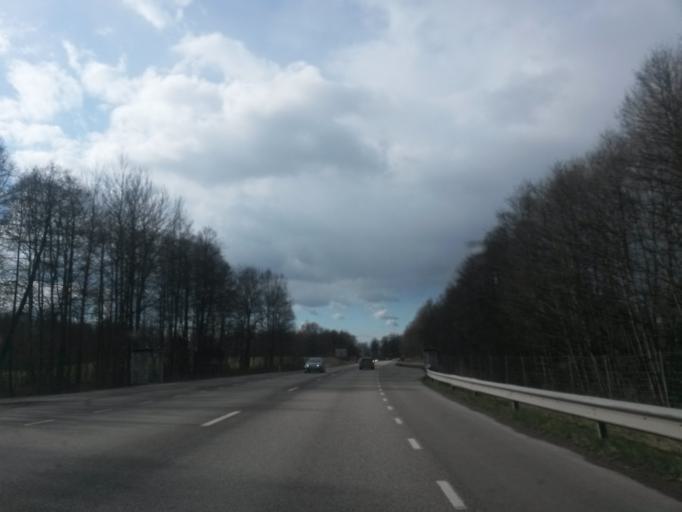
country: SE
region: Vaestra Goetaland
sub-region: Skara Kommun
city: Axvall
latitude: 58.3804
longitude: 13.6848
